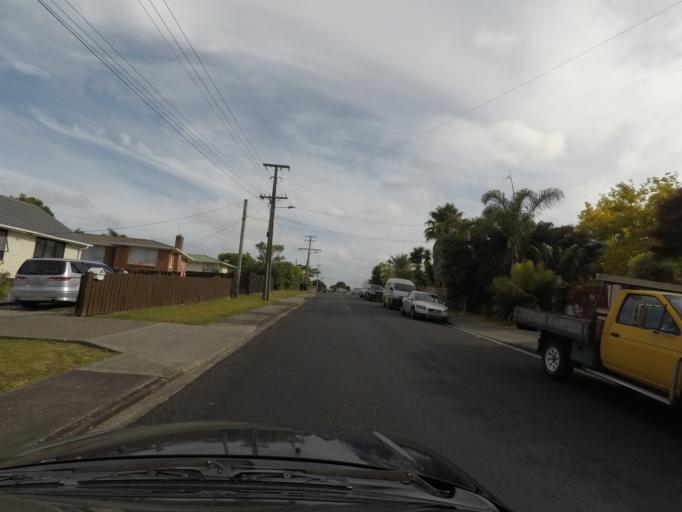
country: NZ
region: Auckland
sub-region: Auckland
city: Rosebank
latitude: -36.8936
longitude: 174.6669
